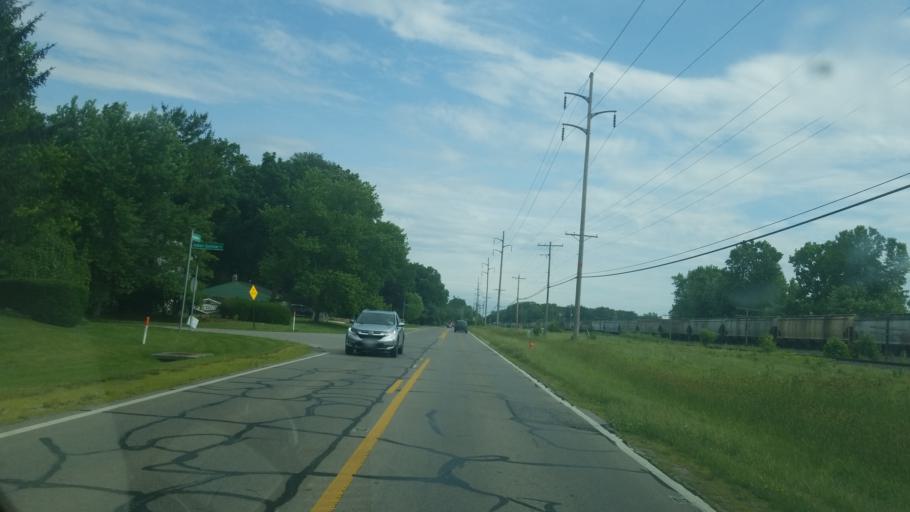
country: US
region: Ohio
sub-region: Franklin County
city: Worthington
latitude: 40.0710
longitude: -83.0008
